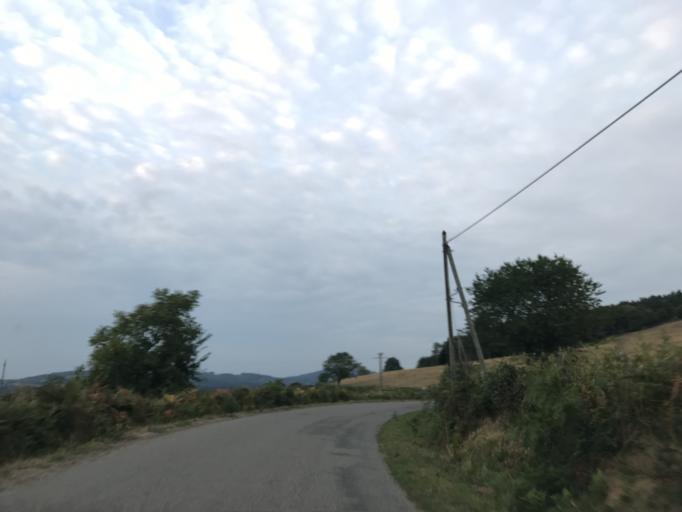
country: FR
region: Auvergne
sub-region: Departement du Puy-de-Dome
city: Thiers
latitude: 45.8486
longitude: 3.5739
